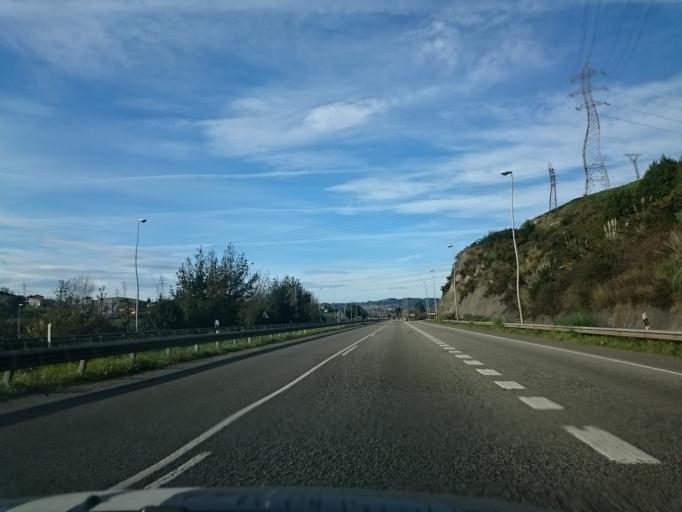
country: ES
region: Asturias
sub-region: Province of Asturias
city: Natahoyo
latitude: 43.5155
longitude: -5.6886
